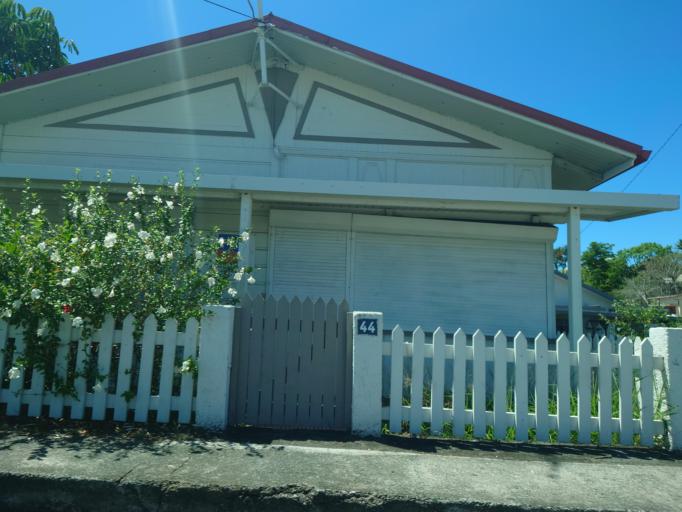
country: NC
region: South Province
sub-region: Noumea
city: Noumea
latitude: -22.2708
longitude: 166.4530
